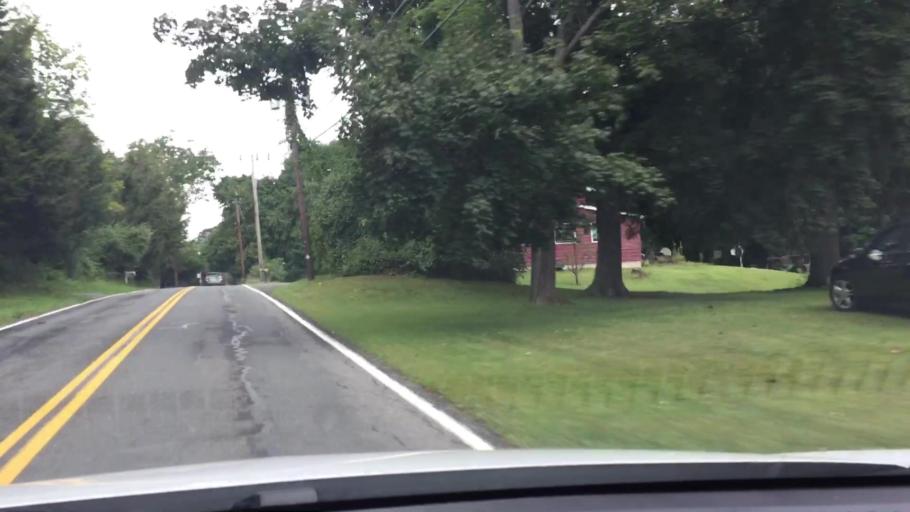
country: US
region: Massachusetts
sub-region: Berkshire County
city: Housatonic
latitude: 42.2530
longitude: -73.3753
